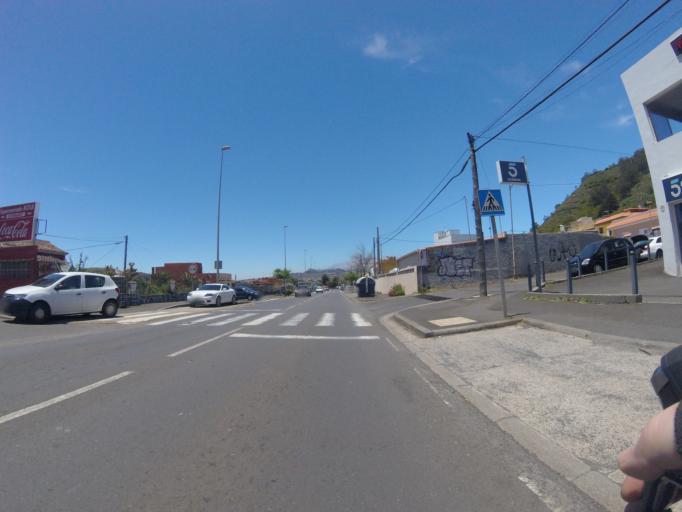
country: ES
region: Canary Islands
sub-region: Provincia de Santa Cruz de Tenerife
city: Tegueste
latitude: 28.5078
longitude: -16.3104
